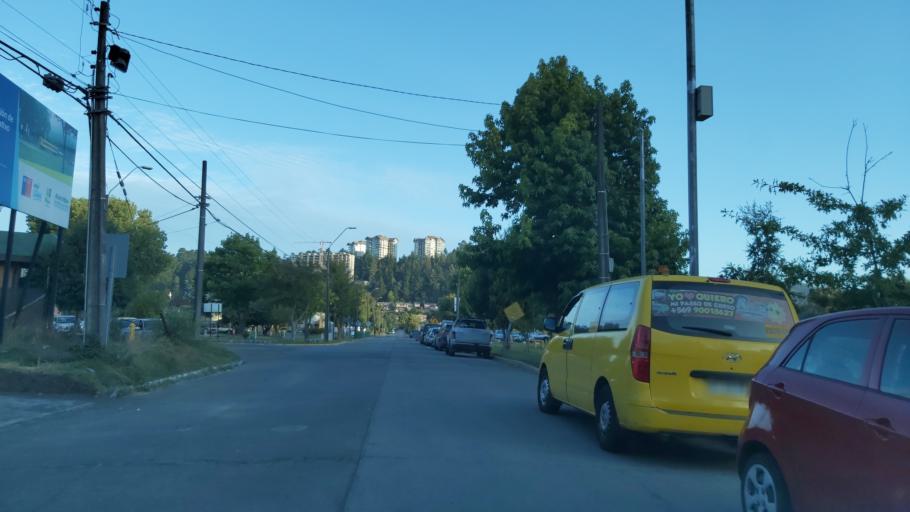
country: CL
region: Biobio
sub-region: Provincia de Concepcion
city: Concepcion
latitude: -36.8460
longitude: -73.1050
